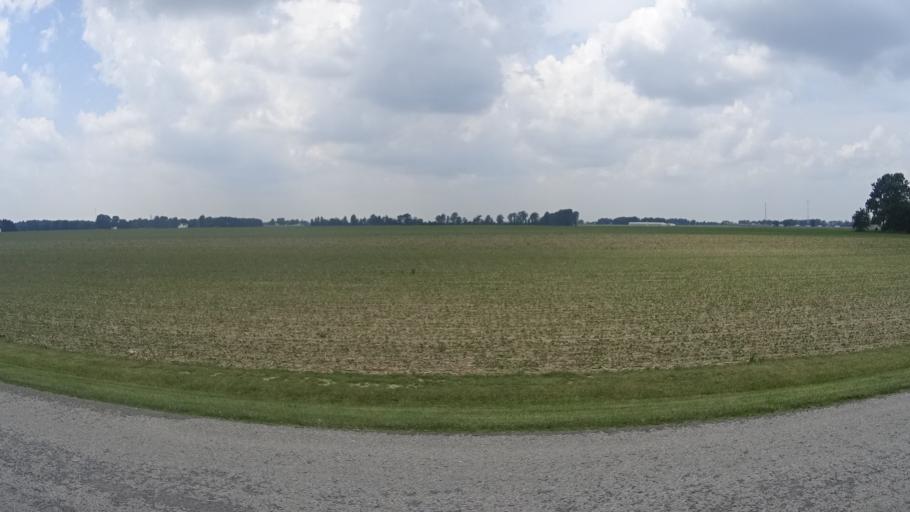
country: US
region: Ohio
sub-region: Erie County
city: Milan
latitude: 41.3279
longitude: -82.6736
